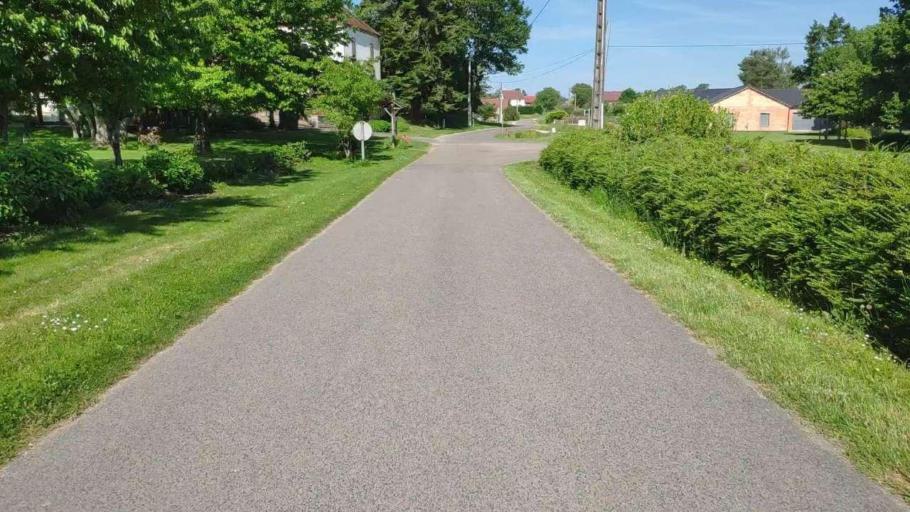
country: FR
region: Franche-Comte
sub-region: Departement du Jura
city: Bletterans
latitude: 46.7073
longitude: 5.4615
